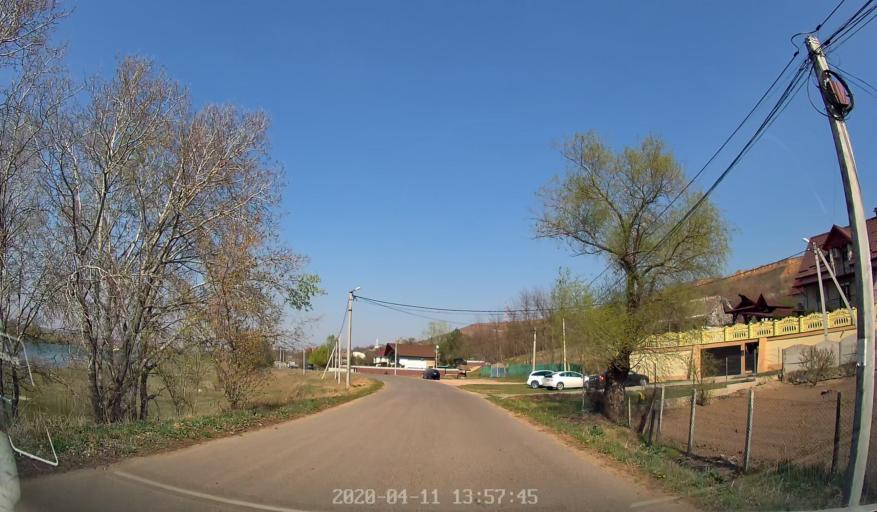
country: MD
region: Chisinau
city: Vadul lui Voda
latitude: 47.0764
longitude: 29.1284
